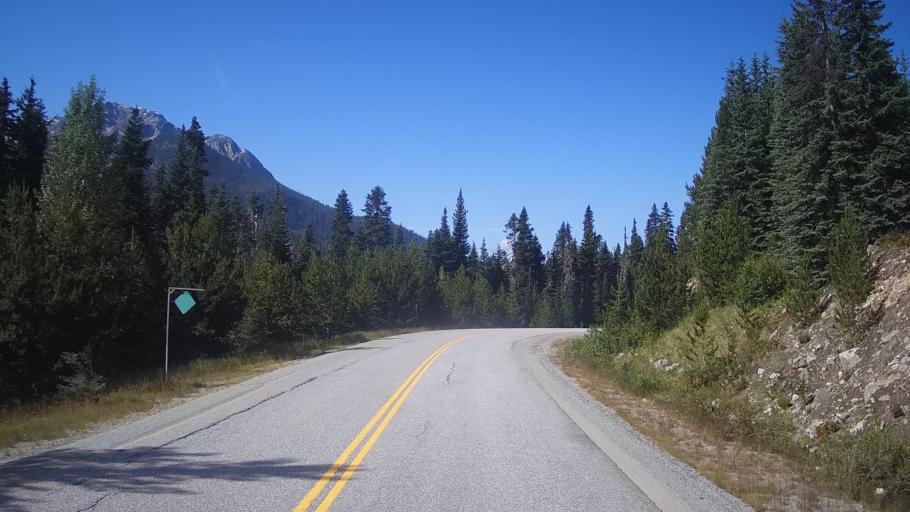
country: CA
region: British Columbia
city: Pemberton
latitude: 50.3804
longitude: -122.4805
